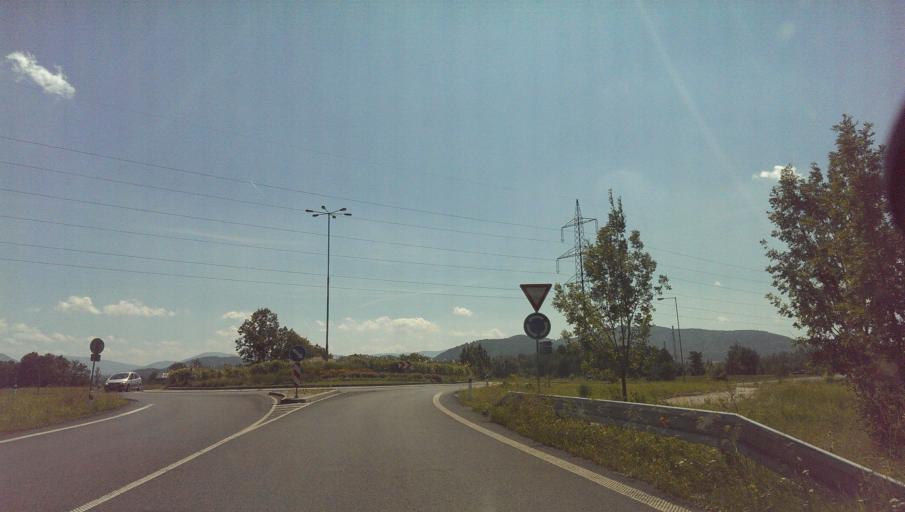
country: CZ
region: Moravskoslezsky
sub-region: Okres Novy Jicin
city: Pribor
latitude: 49.6231
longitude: 18.1501
